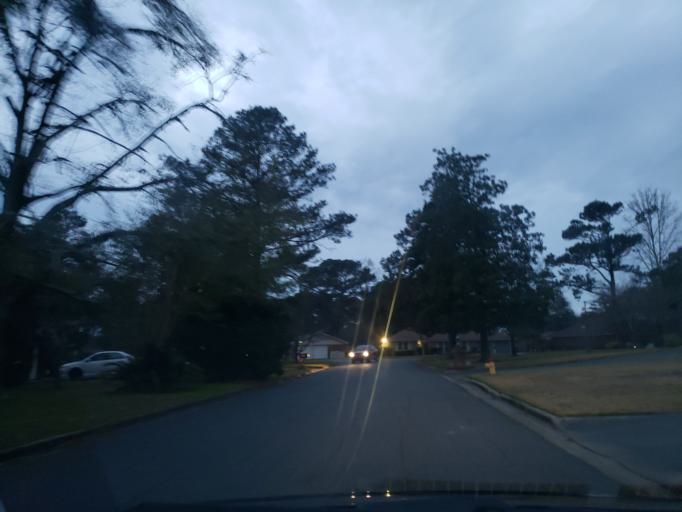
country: US
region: Georgia
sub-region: Chatham County
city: Montgomery
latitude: 31.9924
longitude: -81.1490
